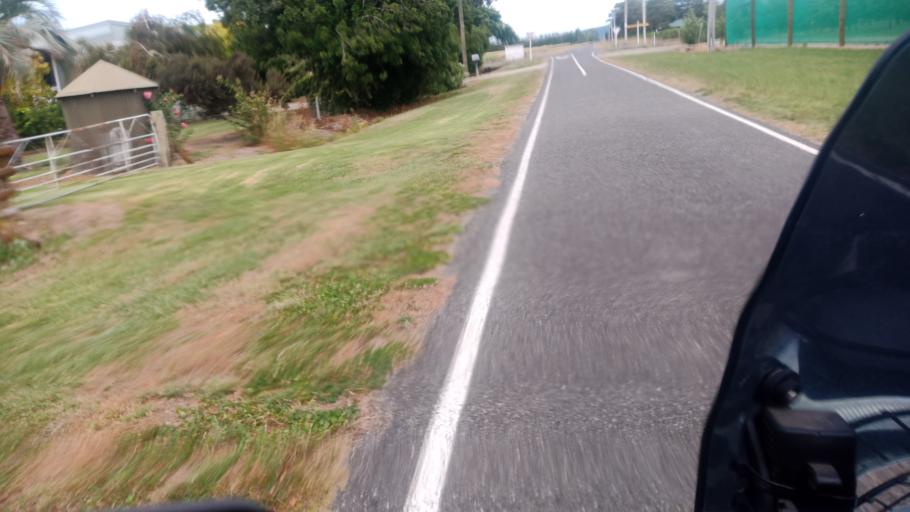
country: NZ
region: Gisborne
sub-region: Gisborne District
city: Gisborne
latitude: -38.6311
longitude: 177.8812
